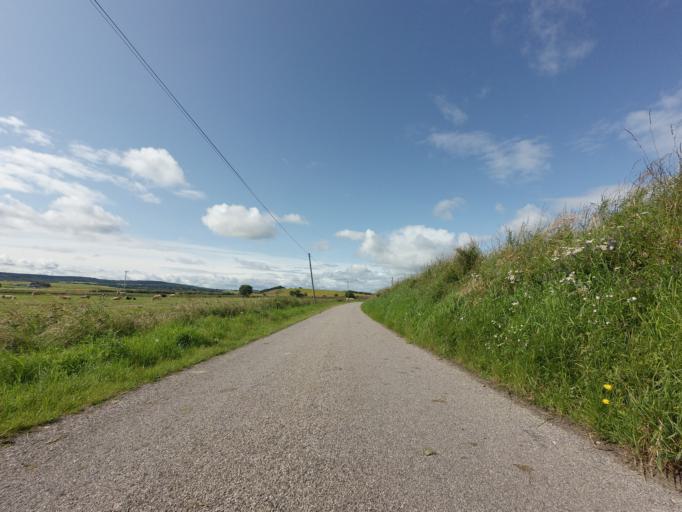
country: GB
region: Scotland
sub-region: Moray
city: Burghead
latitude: 57.6487
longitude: -3.5062
